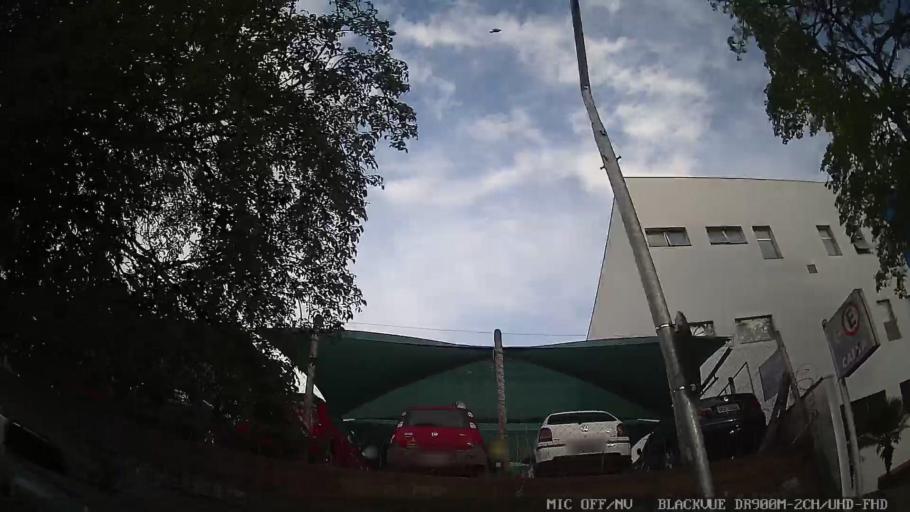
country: BR
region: Sao Paulo
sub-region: Braganca Paulista
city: Braganca Paulista
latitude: -22.9469
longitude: -46.5410
